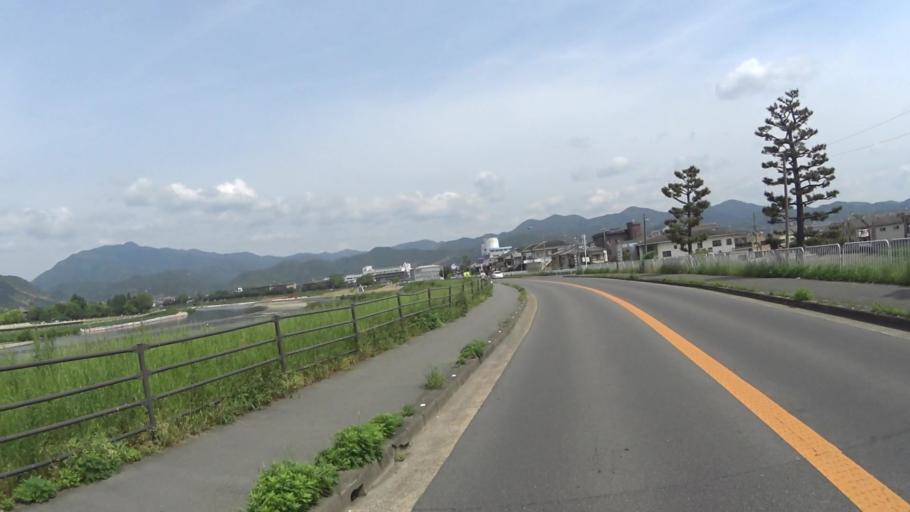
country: JP
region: Kyoto
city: Muko
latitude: 35.0057
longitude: 135.6905
